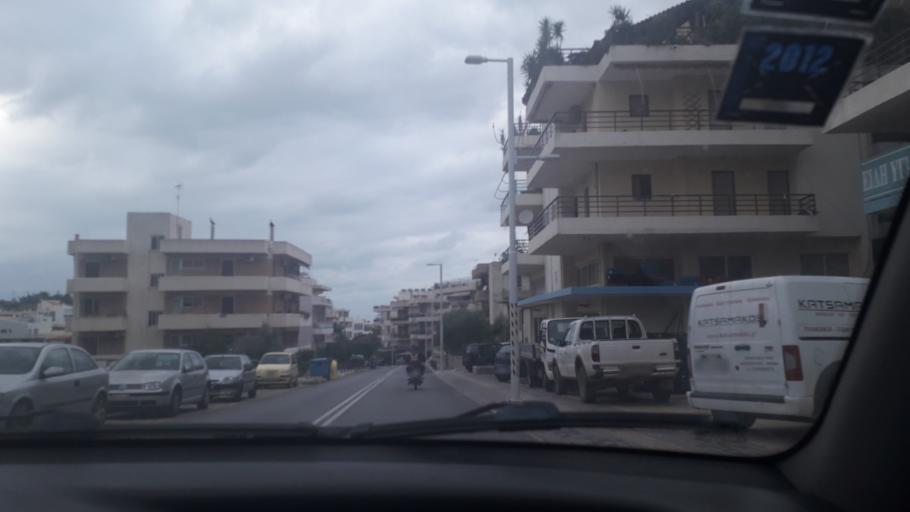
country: GR
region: Crete
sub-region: Nomos Rethymnis
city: Rethymno
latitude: 35.3604
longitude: 24.4745
